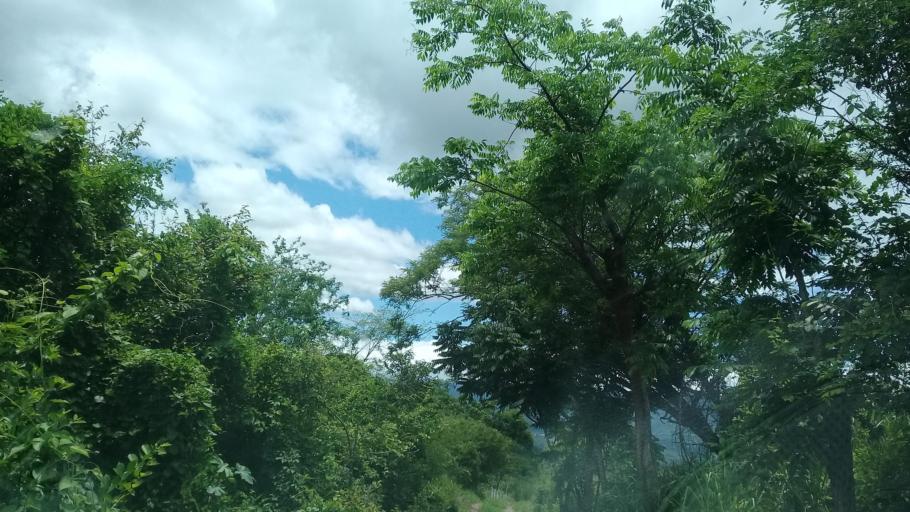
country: MX
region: Veracruz
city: El Castillo
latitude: 19.5744
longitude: -96.8350
